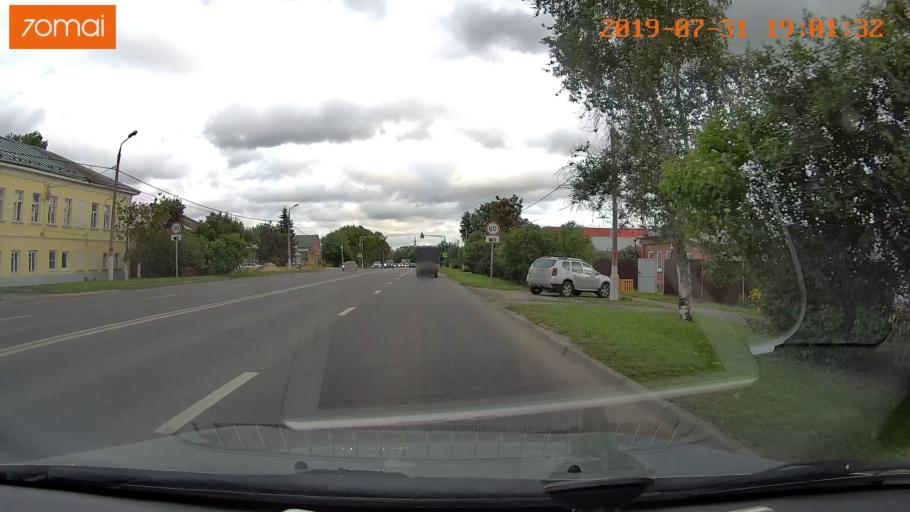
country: RU
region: Moskovskaya
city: Raduzhnyy
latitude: 55.1258
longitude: 38.7290
